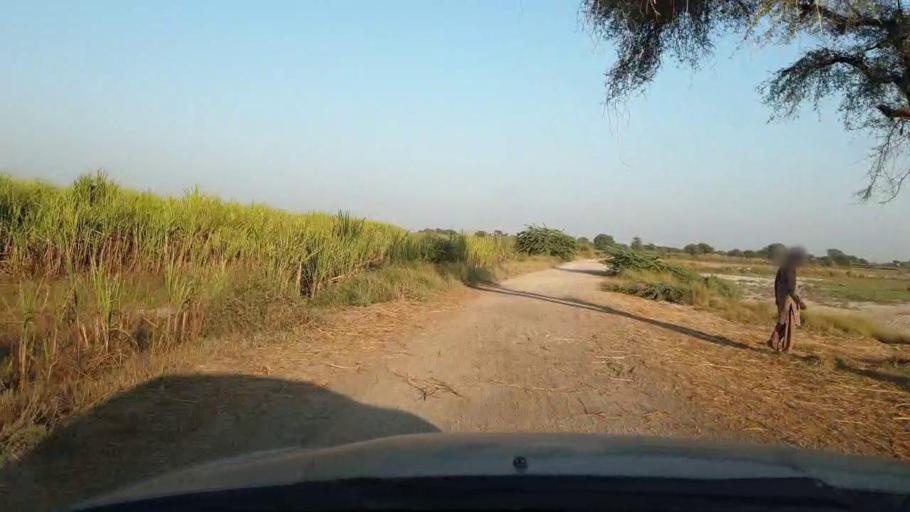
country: PK
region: Sindh
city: Matli
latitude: 25.0319
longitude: 68.6242
